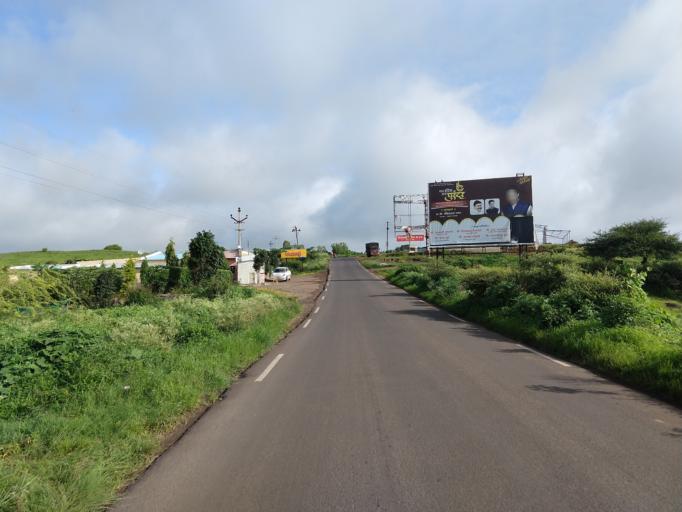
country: IN
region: Maharashtra
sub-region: Pune Division
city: Khed
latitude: 18.3979
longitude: 73.9142
